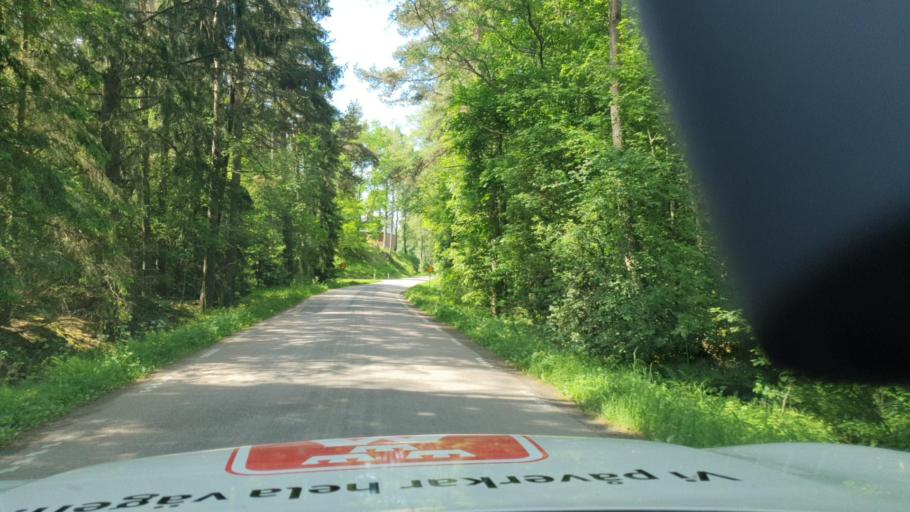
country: SE
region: Vaestra Goetaland
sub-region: Herrljunga Kommun
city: Herrljunga
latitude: 57.9305
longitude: 13.0483
